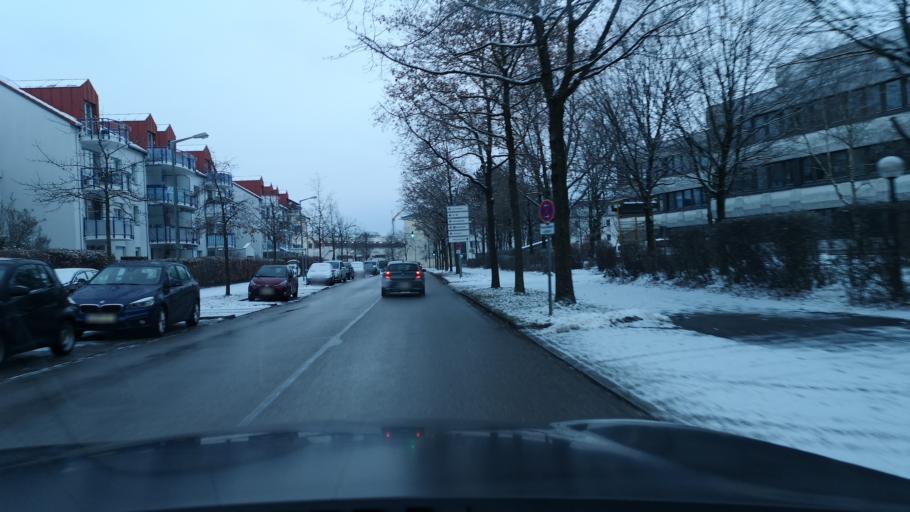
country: DE
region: Bavaria
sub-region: Upper Bavaria
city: Poing
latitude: 48.1724
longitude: 11.8046
